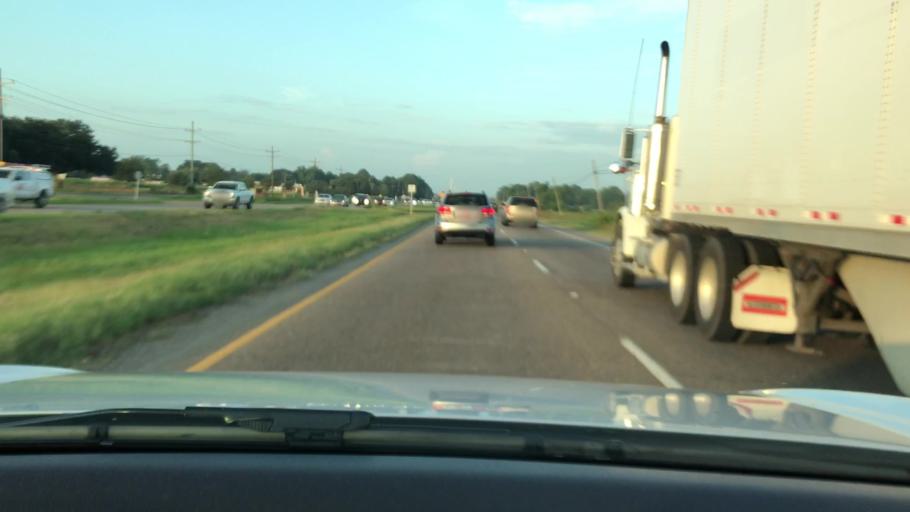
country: US
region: Louisiana
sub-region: West Baton Rouge Parish
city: Brusly
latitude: 30.3976
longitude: -91.2367
